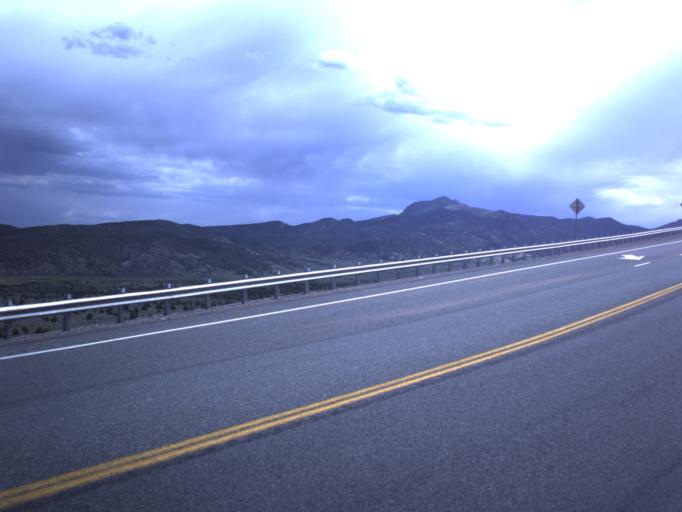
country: US
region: Utah
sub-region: Garfield County
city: Panguitch
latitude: 38.0250
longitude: -112.5192
